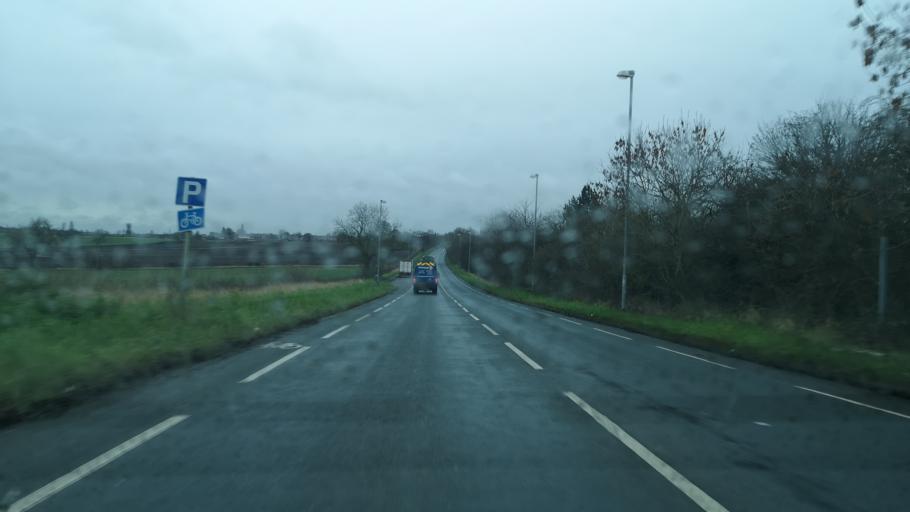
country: GB
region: England
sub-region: City and Borough of Wakefield
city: Crofton
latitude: 53.6656
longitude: -1.4309
